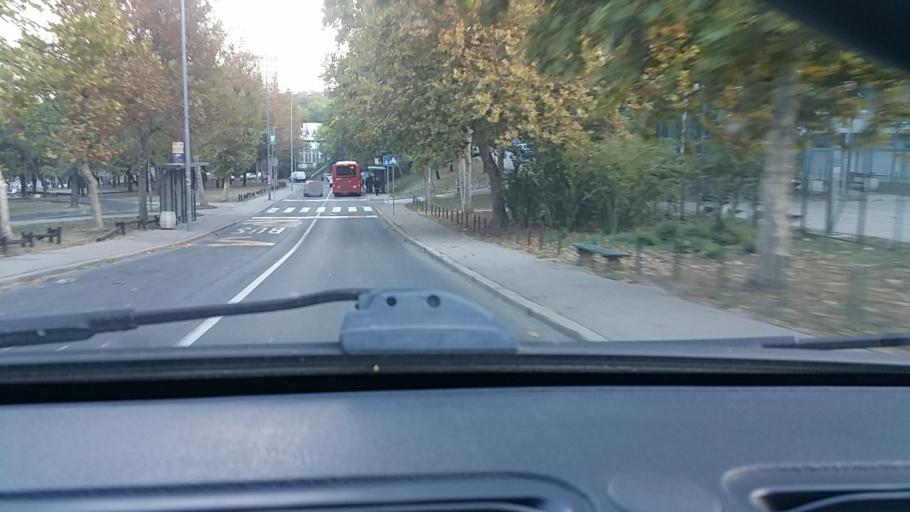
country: RS
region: Central Serbia
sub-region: Belgrade
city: Rakovica
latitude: 44.7477
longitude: 20.4568
